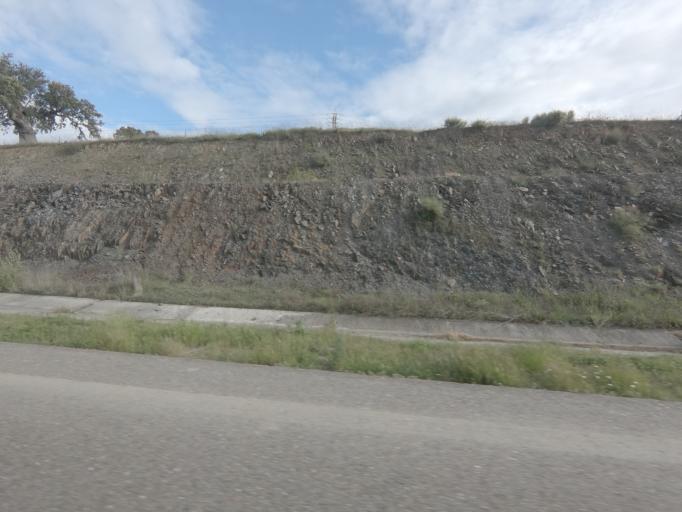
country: ES
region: Extremadura
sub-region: Provincia de Caceres
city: Casas de Don Gomez
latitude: 40.0264
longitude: -6.6109
